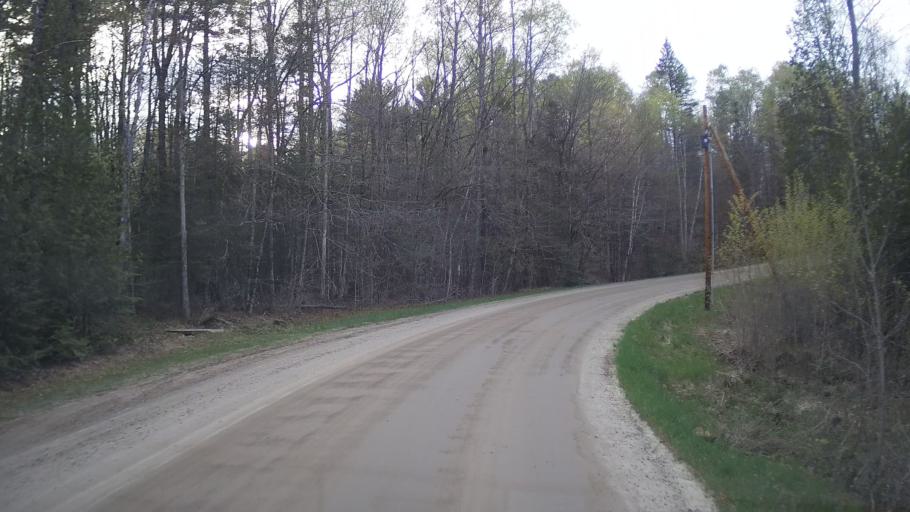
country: US
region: Vermont
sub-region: Caledonia County
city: Lyndonville
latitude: 44.5957
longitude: -71.9588
